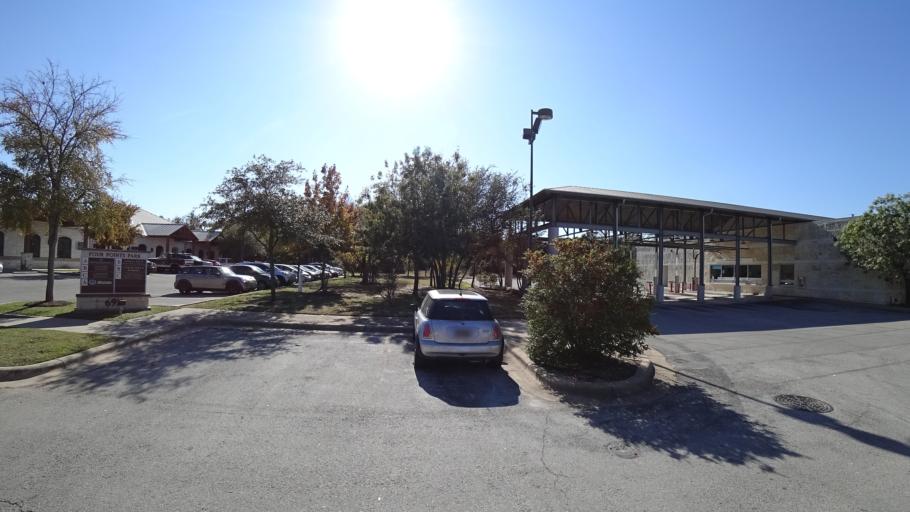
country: US
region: Texas
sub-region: Williamson County
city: Anderson Mill
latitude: 30.4018
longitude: -97.8537
